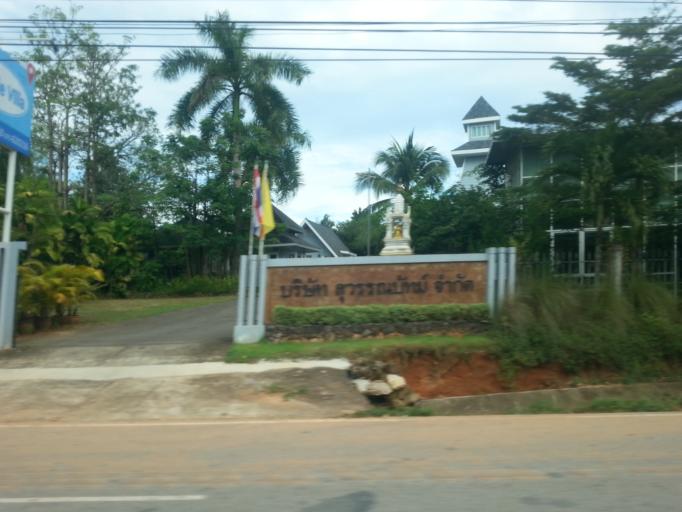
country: TH
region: Krabi
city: Krabi
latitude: 8.0889
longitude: 98.8928
